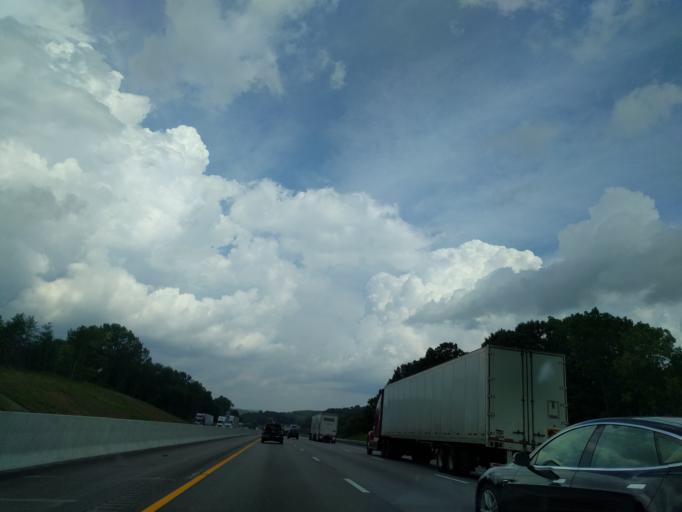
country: US
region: Kentucky
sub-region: Hart County
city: Munfordville
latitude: 37.3263
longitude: -85.9065
